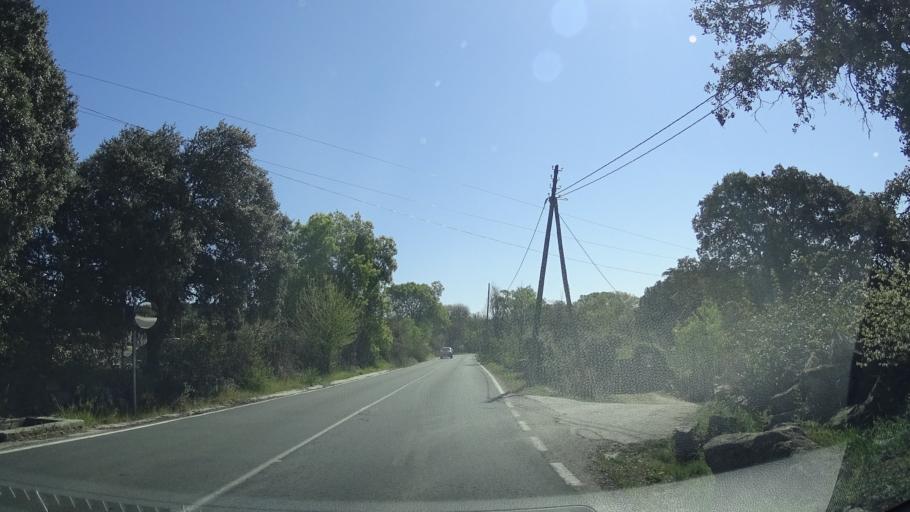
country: ES
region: Madrid
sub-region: Provincia de Madrid
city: Hoyo de Manzanares
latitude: 40.6238
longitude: -3.8983
